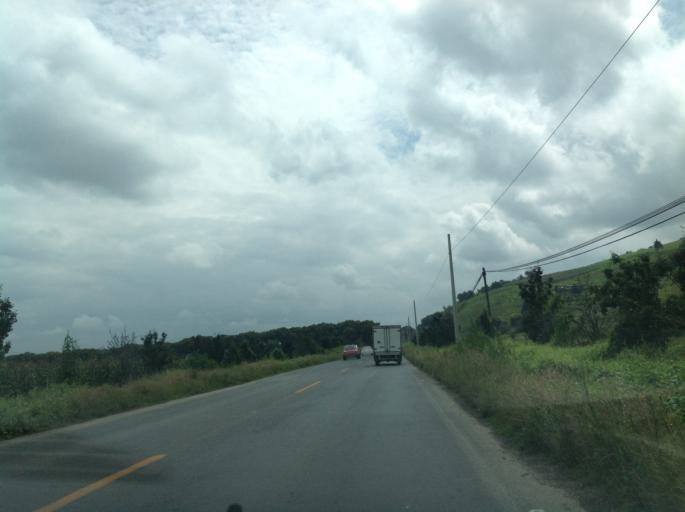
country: MX
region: Mexico
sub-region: Rayon
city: Colonia Emiliano Zapata
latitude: 19.1126
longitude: -99.5666
